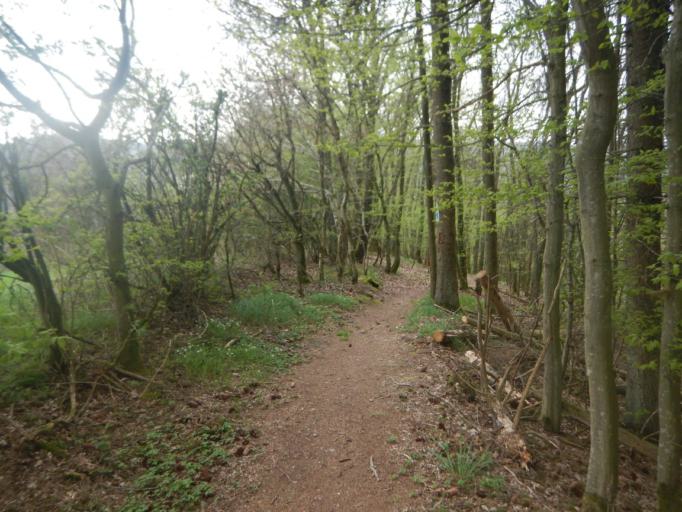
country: LU
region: Diekirch
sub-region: Canton de Wiltz
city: Esch-sur-Sure
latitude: 49.9118
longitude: 5.9399
